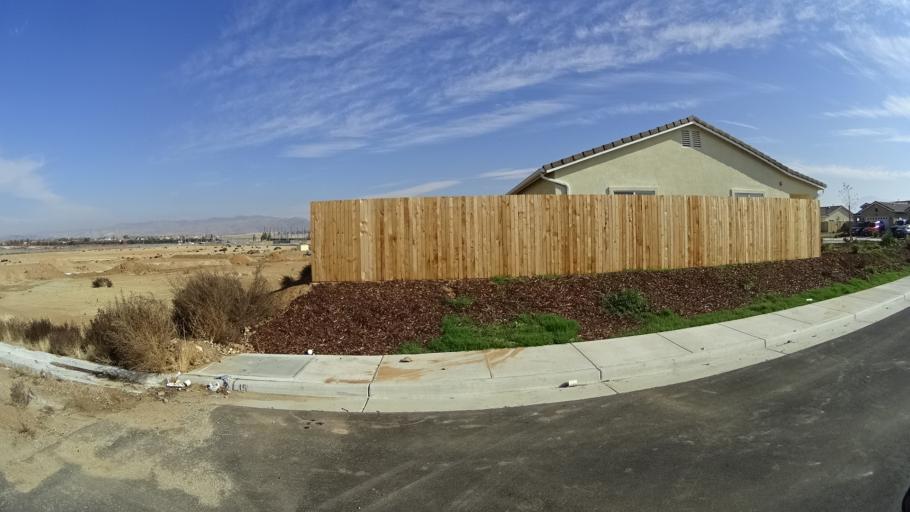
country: US
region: California
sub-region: Kern County
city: Bakersfield
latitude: 35.3945
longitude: -118.8937
